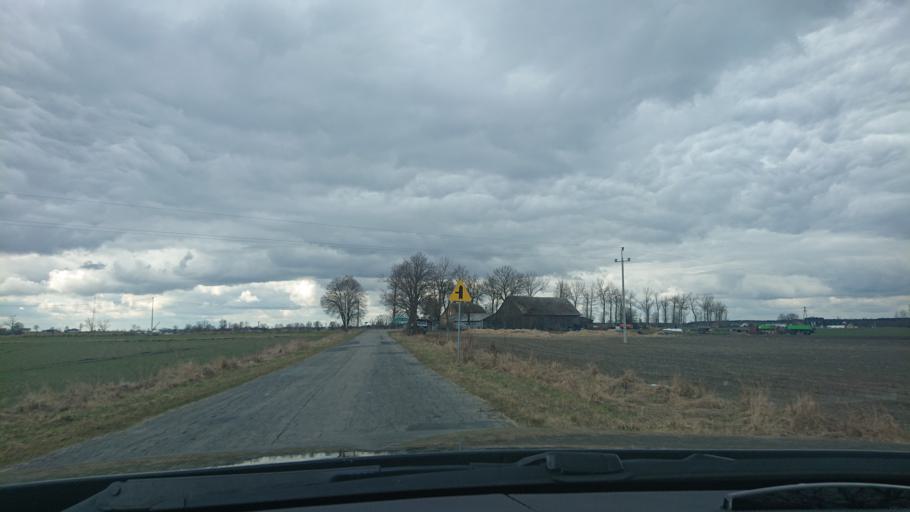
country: PL
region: Greater Poland Voivodeship
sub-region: Powiat gnieznienski
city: Trzemeszno
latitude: 52.5840
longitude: 17.7039
